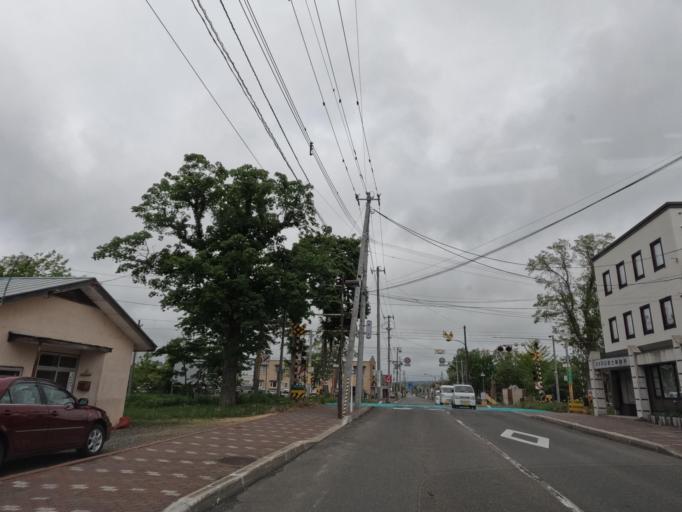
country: JP
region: Hokkaido
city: Tobetsu
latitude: 43.2229
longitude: 141.5183
